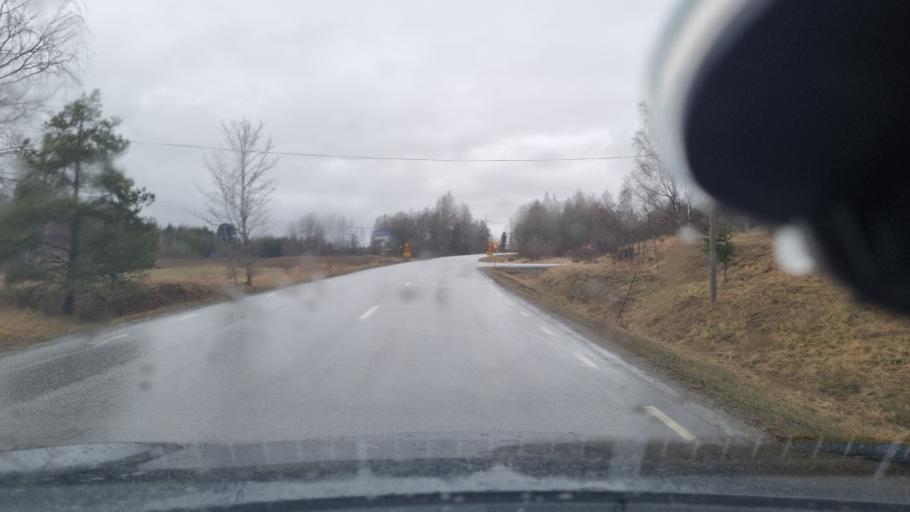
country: SE
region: Stockholm
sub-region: Upplands-Bro Kommun
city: Kungsaengen
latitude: 59.5255
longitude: 17.7521
